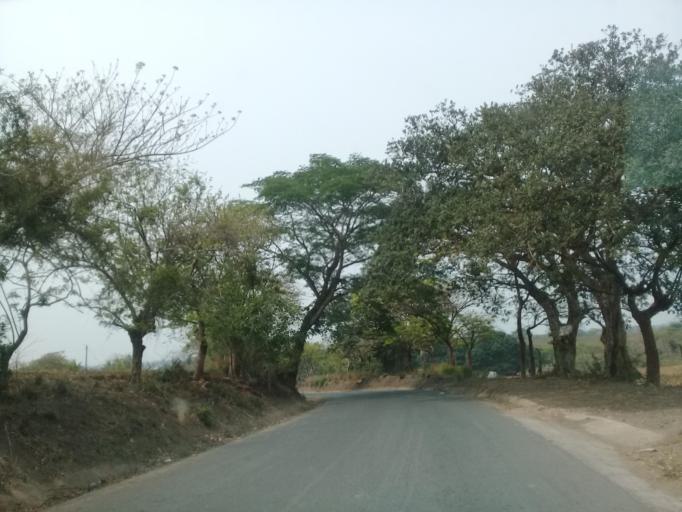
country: MX
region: Veracruz
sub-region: Medellin
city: La Laguna y Monte del Castillo
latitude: 18.9589
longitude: -96.1219
